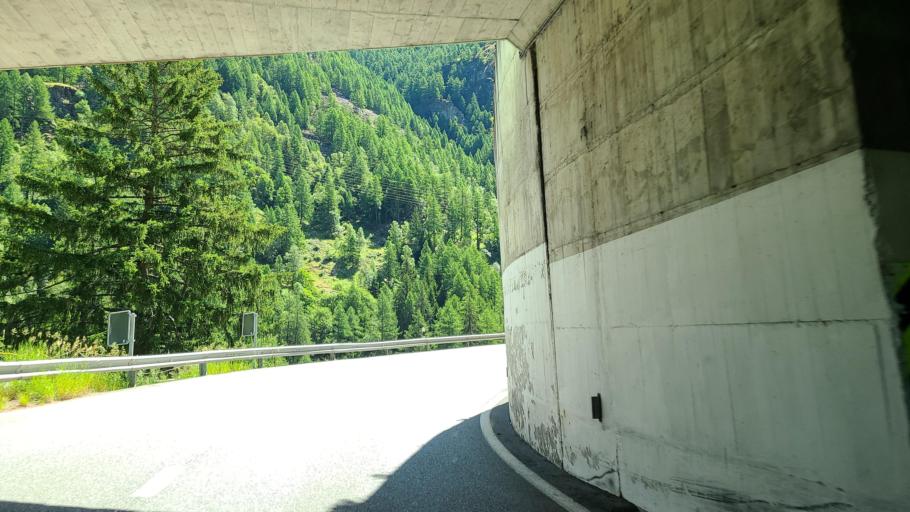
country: CH
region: Valais
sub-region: Visp District
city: Stalden
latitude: 46.1857
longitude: 7.9015
